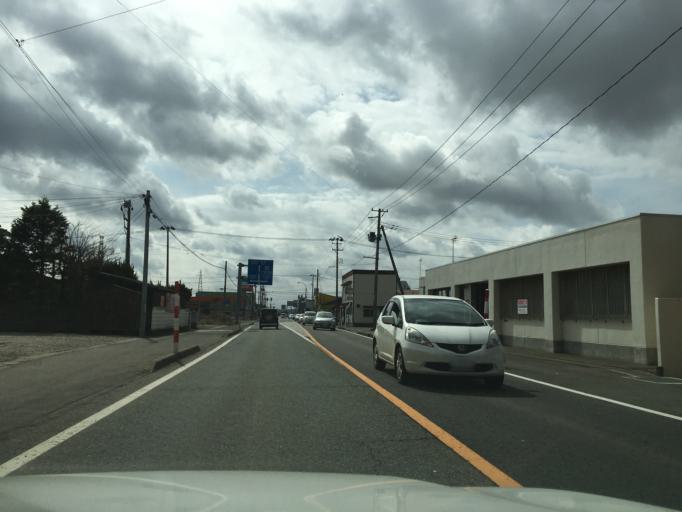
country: JP
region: Akita
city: Tenno
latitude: 39.9459
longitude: 140.0837
